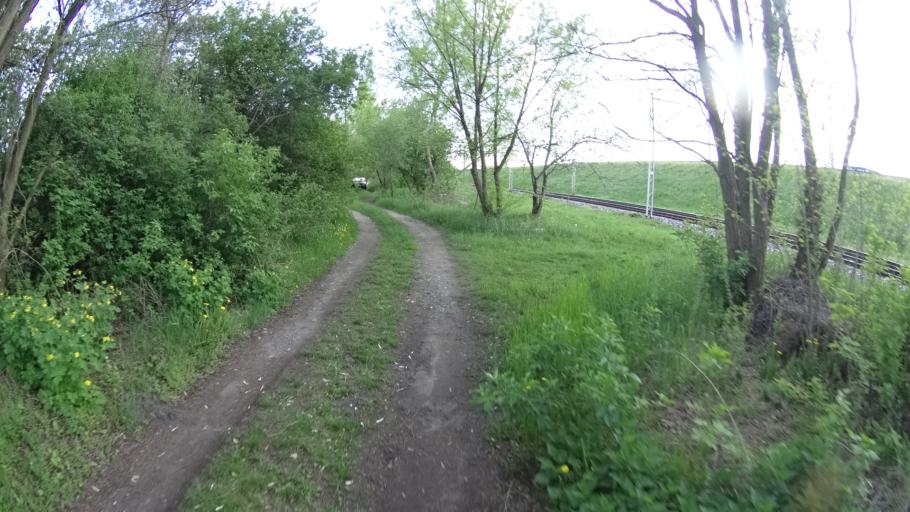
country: PL
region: Masovian Voivodeship
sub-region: Warszawa
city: Wlochy
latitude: 52.2123
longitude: 20.9401
